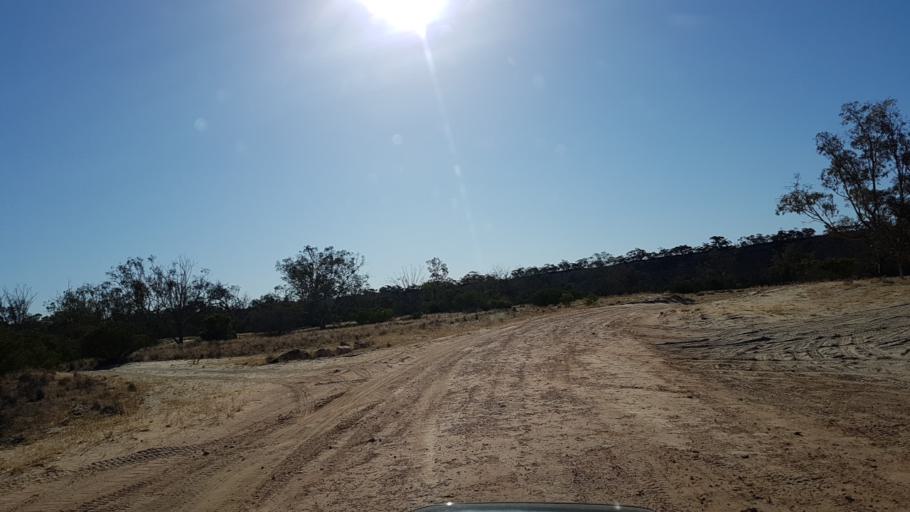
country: AU
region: South Australia
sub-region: Loxton Waikerie
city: Waikerie
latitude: -34.1565
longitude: 140.0229
